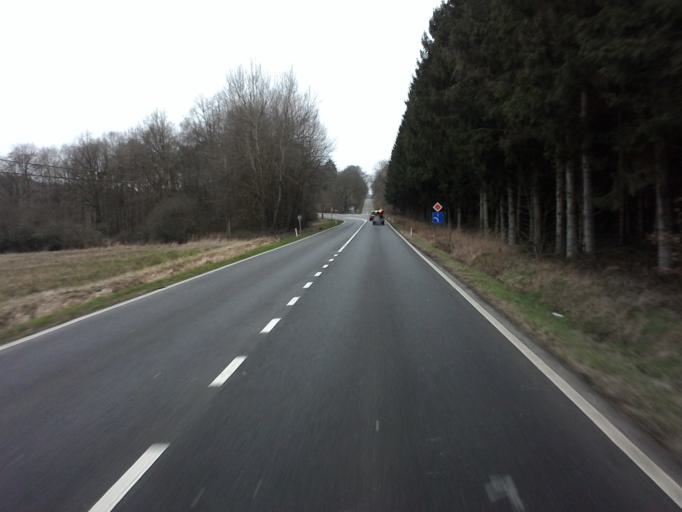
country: BE
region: Wallonia
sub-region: Province de Namur
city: Beauraing
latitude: 50.0493
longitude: 4.9720
